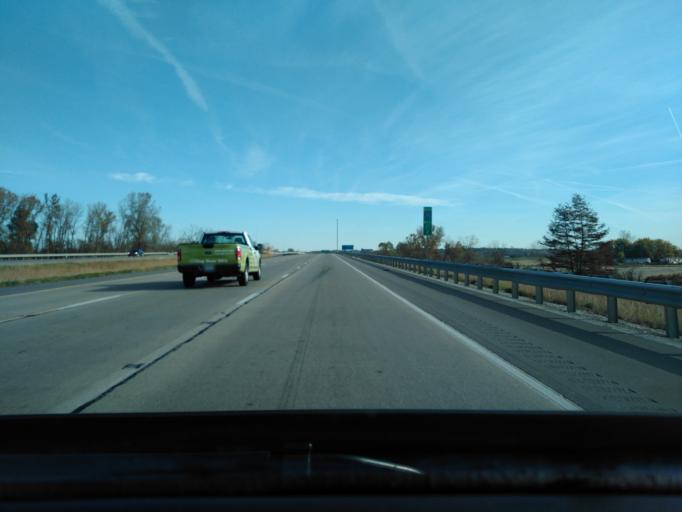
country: US
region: Illinois
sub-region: Saint Clair County
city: Caseyville
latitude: 38.6384
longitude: -90.0549
